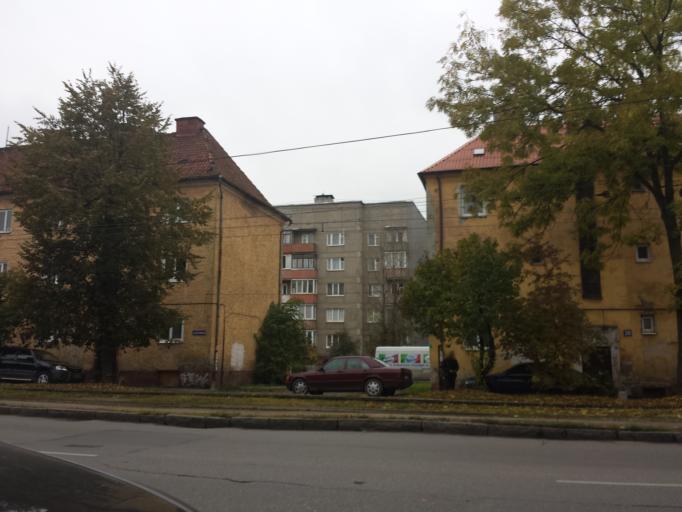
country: RU
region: Kaliningrad
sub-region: Gorod Kaliningrad
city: Kaliningrad
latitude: 54.6901
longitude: 20.5235
